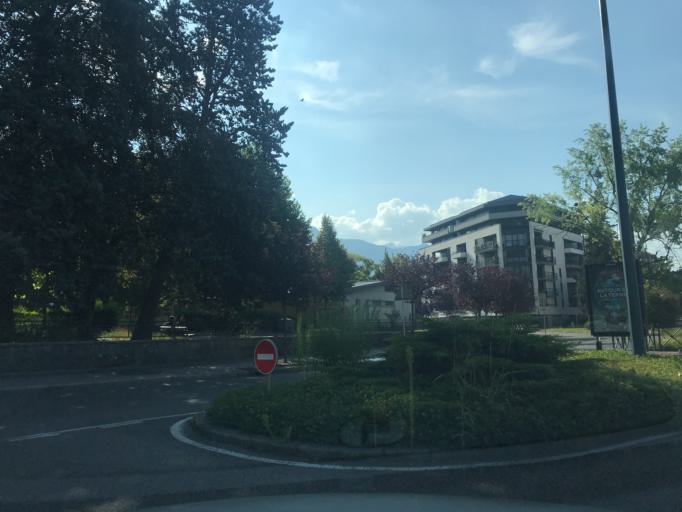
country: FR
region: Rhone-Alpes
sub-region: Departement de la Haute-Savoie
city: Annecy-le-Vieux
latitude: 45.9083
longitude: 6.1356
